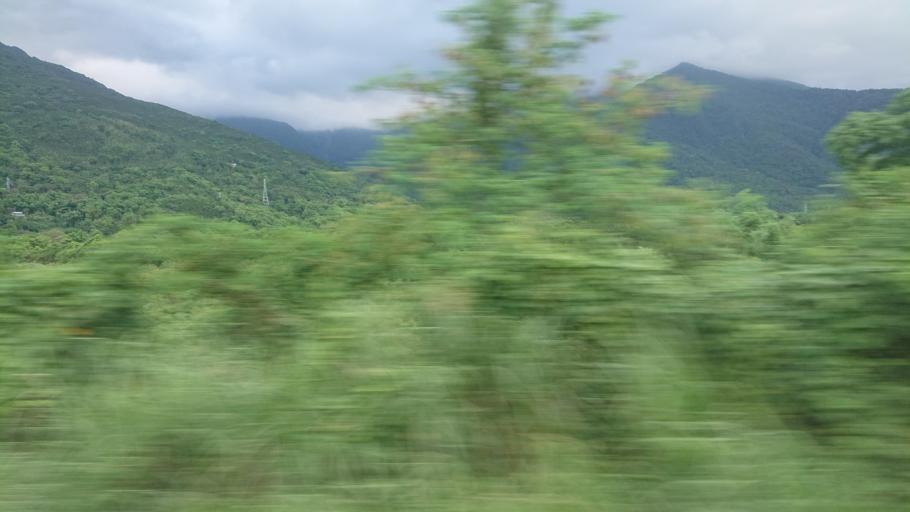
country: TW
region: Taiwan
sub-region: Hualien
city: Hualian
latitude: 23.6255
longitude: 121.3999
